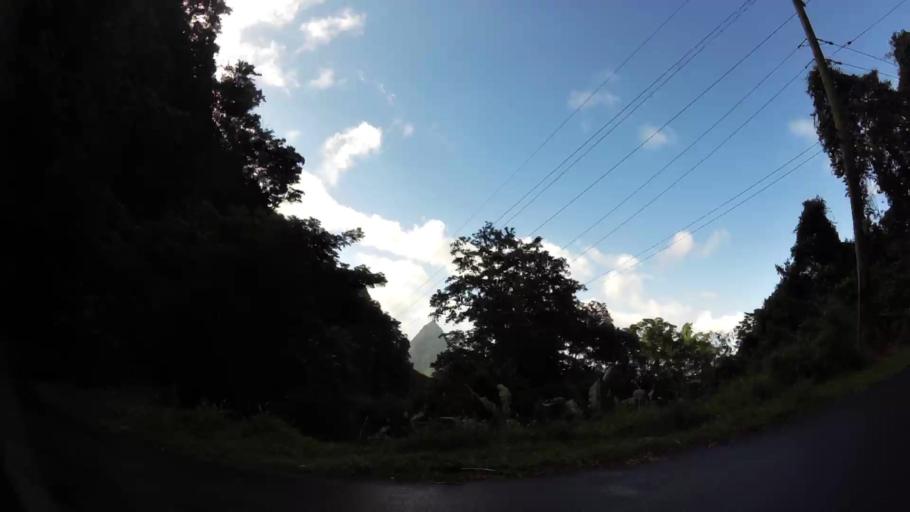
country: LC
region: Soufriere
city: Soufriere
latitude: 13.8738
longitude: -61.0420
